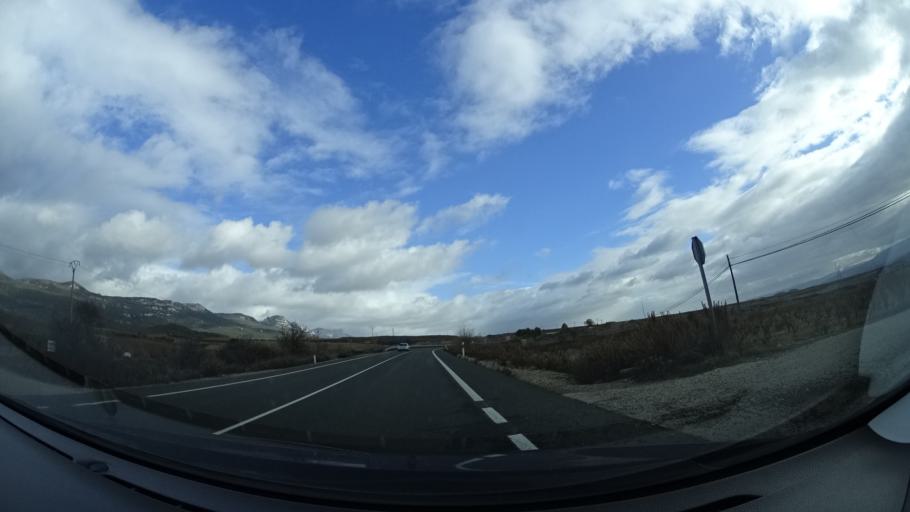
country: ES
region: La Rioja
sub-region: Provincia de La Rioja
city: San Vicente de la Sonsierra
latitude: 42.5666
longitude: -2.7368
